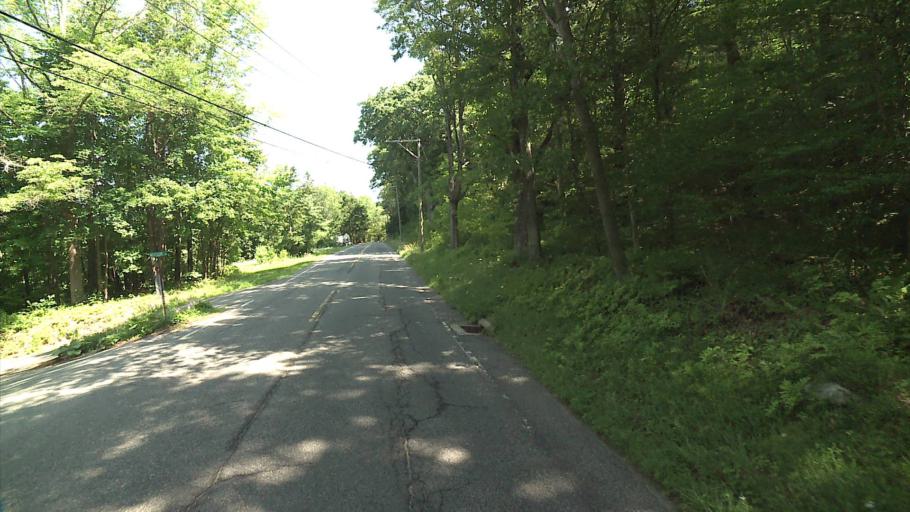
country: US
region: Connecticut
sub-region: Litchfield County
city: Winchester Center
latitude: 41.9582
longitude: -73.2015
